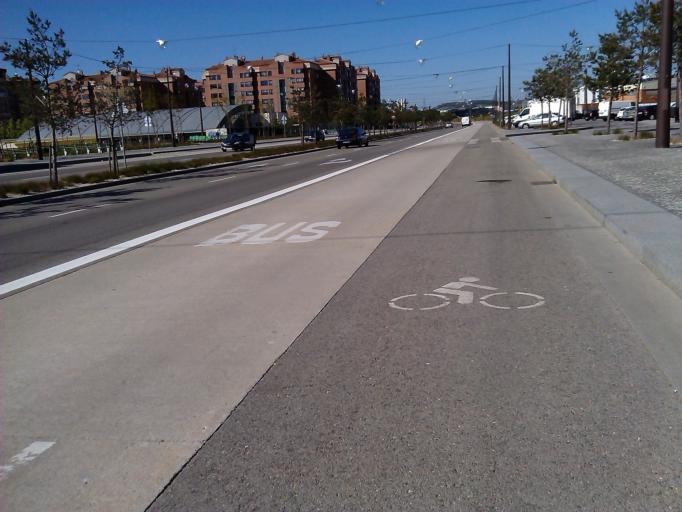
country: ES
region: Castille and Leon
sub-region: Provincia de Burgos
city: Burgos
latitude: 42.3469
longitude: -3.6626
